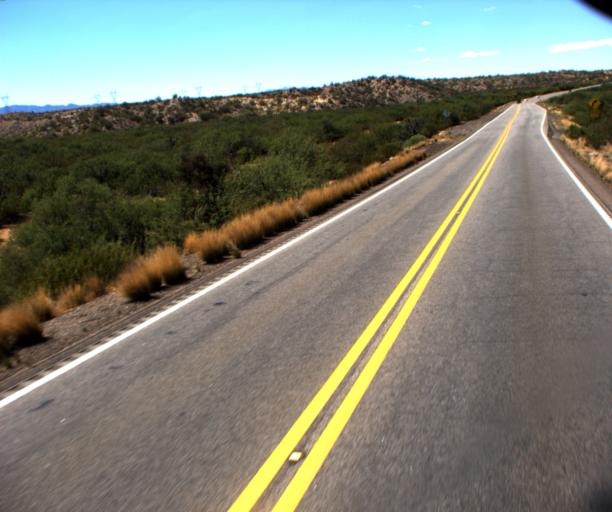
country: US
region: Arizona
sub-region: Yavapai County
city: Bagdad
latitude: 34.7978
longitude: -113.6242
